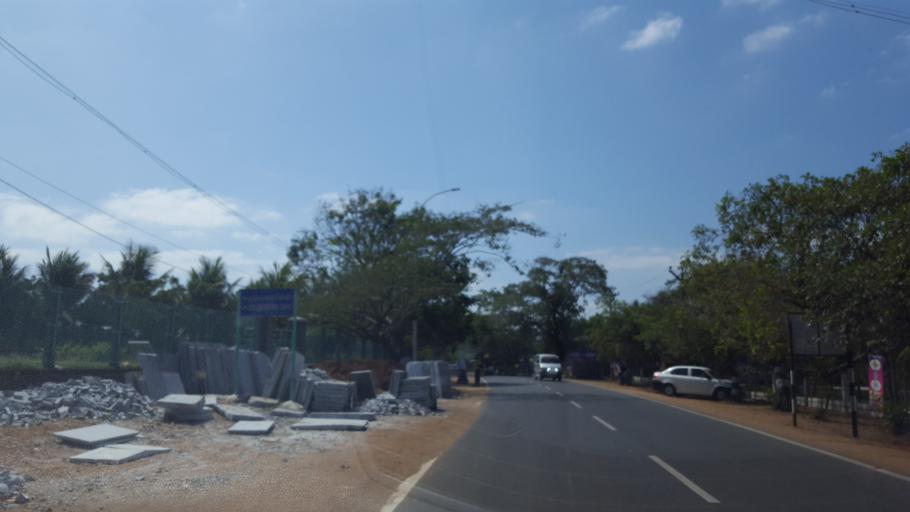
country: IN
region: Tamil Nadu
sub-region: Kancheepuram
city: Mamallapuram
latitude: 12.6275
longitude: 80.1945
